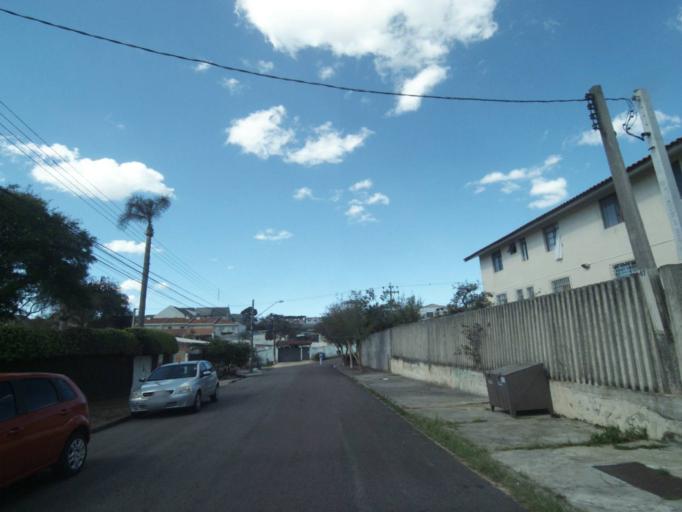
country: BR
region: Parana
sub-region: Curitiba
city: Curitiba
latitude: -25.3788
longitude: -49.2463
